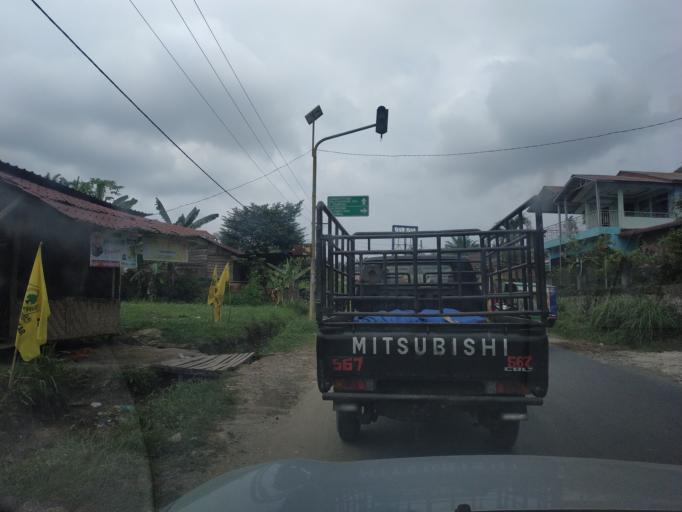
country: ID
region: North Sumatra
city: Kotapinang
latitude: 1.8394
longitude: 100.0135
